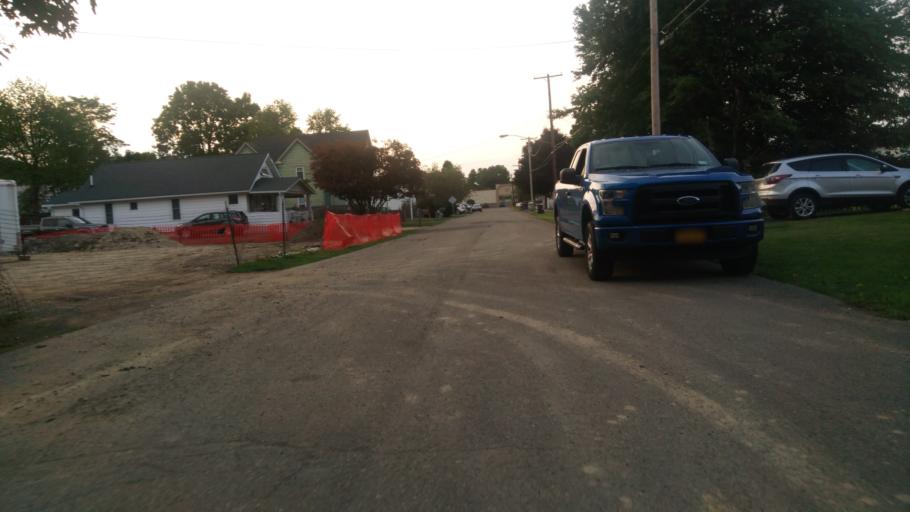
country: US
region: New York
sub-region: Chemung County
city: Southport
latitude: 42.0586
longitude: -76.8104
